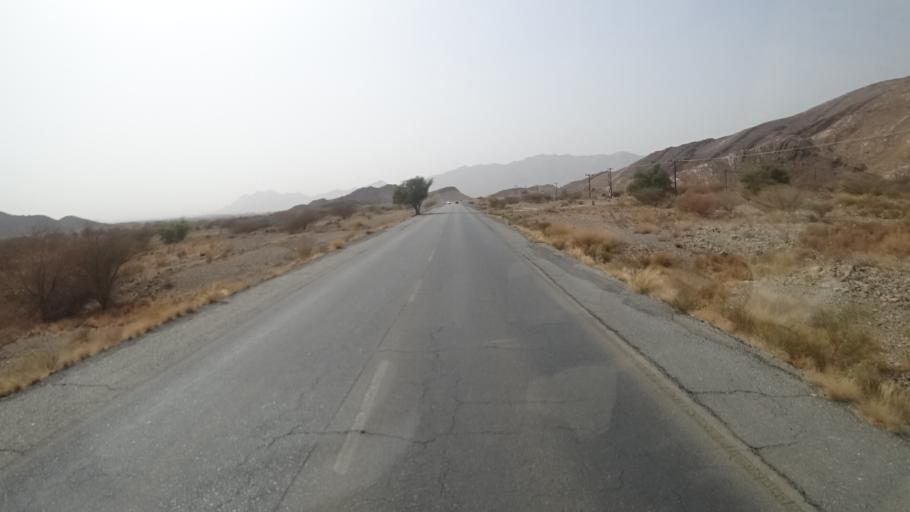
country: OM
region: Muhafazat ad Dakhiliyah
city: Nizwa
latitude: 22.9253
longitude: 57.6394
